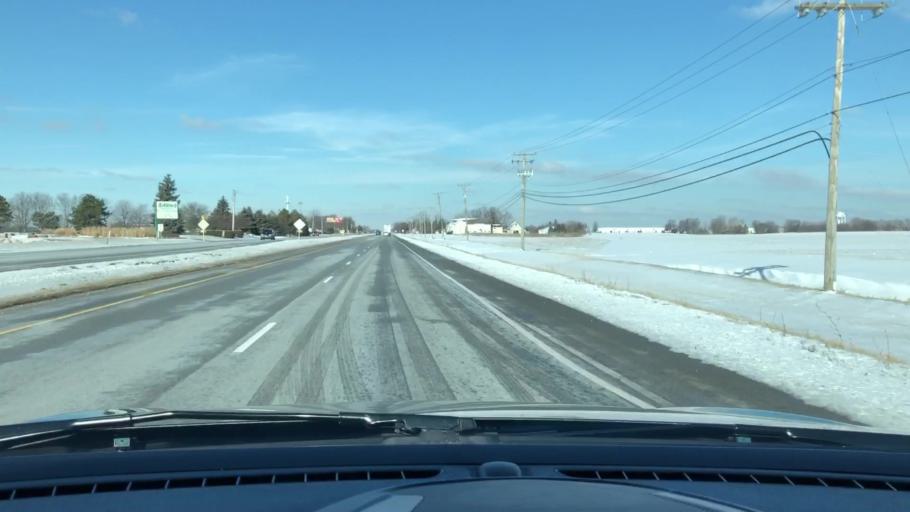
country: US
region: Illinois
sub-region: Will County
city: Preston Heights
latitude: 41.4667
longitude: -88.0796
